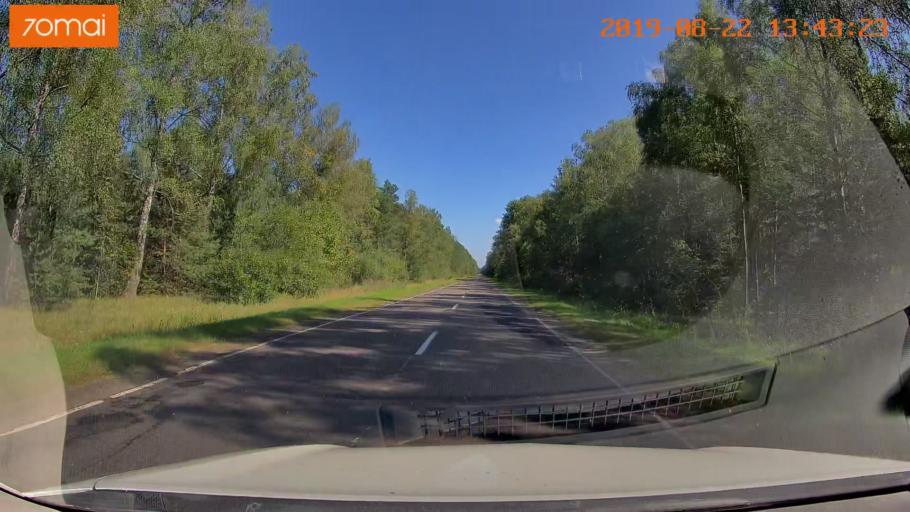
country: BY
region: Mogilev
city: Asipovichy
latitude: 53.2426
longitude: 28.4354
